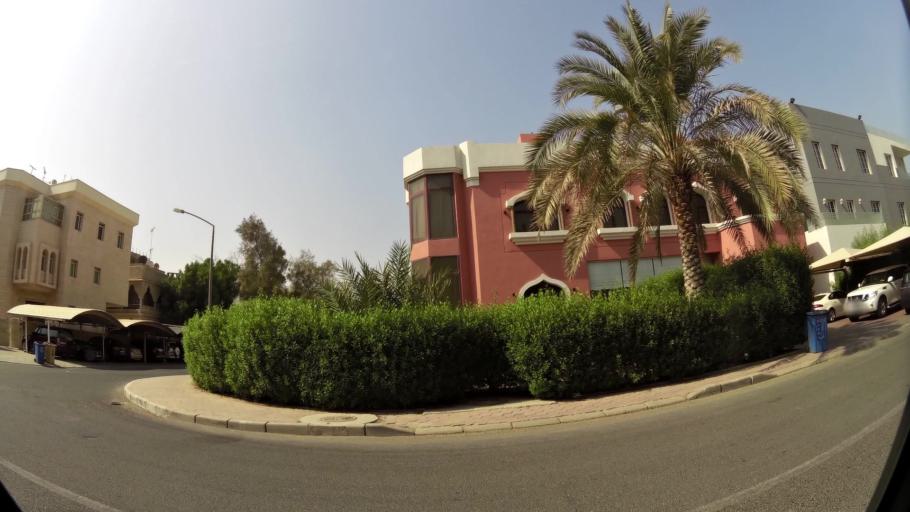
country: KW
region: Al Asimah
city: Ad Dasmah
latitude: 29.3517
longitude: 48.0172
